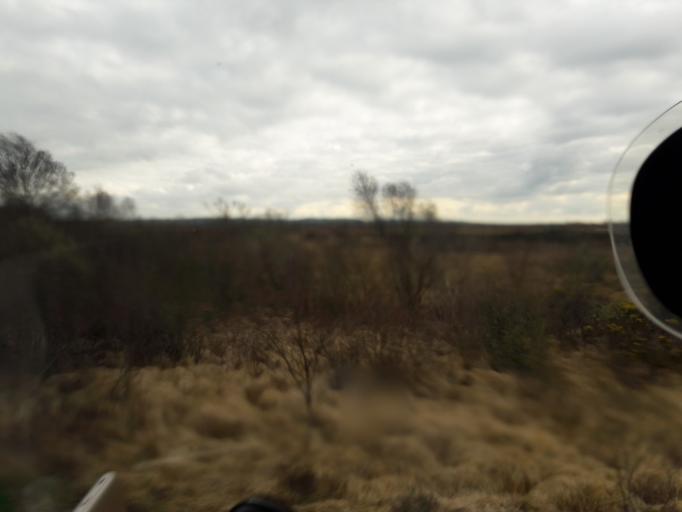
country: IE
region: Leinster
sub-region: An Longfort
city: Granard
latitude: 53.6630
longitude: -7.4621
